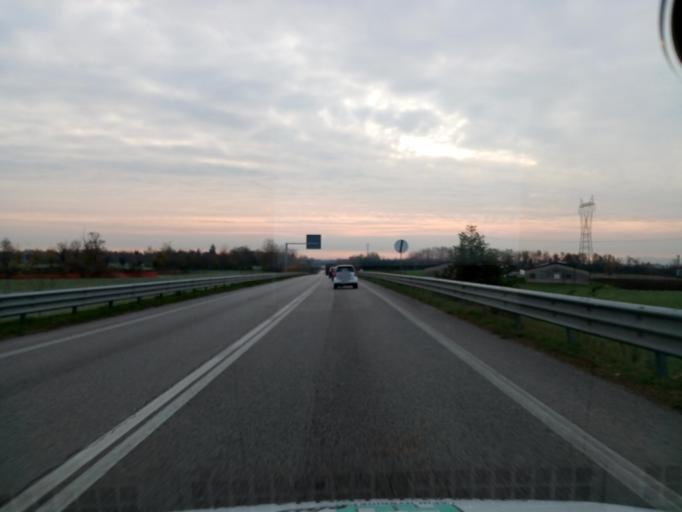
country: IT
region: Veneto
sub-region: Provincia di Vicenza
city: Zane
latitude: 45.7153
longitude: 11.4324
